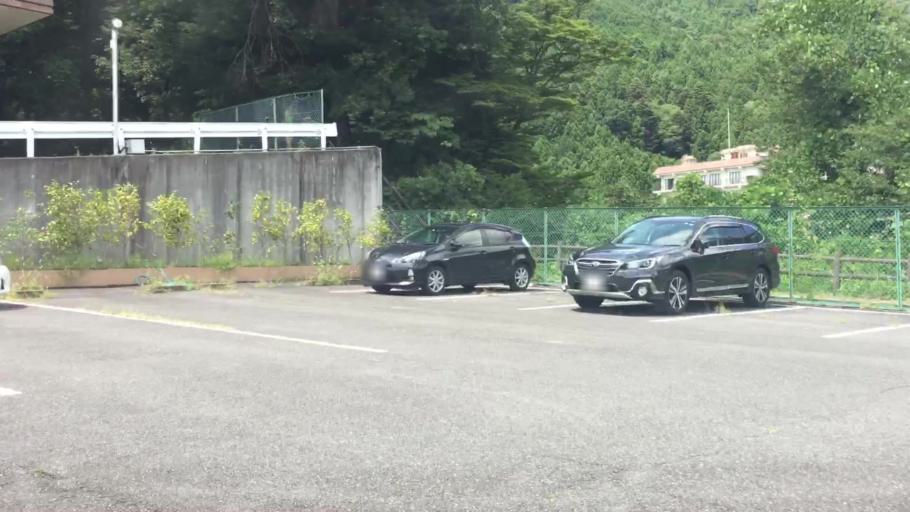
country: JP
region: Tochigi
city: Imaichi
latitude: 36.8235
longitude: 139.7117
